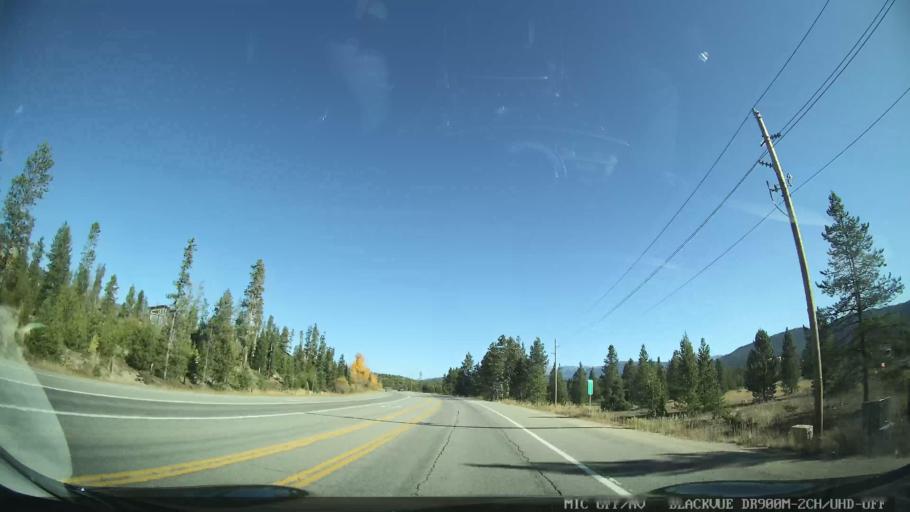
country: US
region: Colorado
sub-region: Grand County
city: Granby
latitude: 40.2062
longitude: -105.8605
